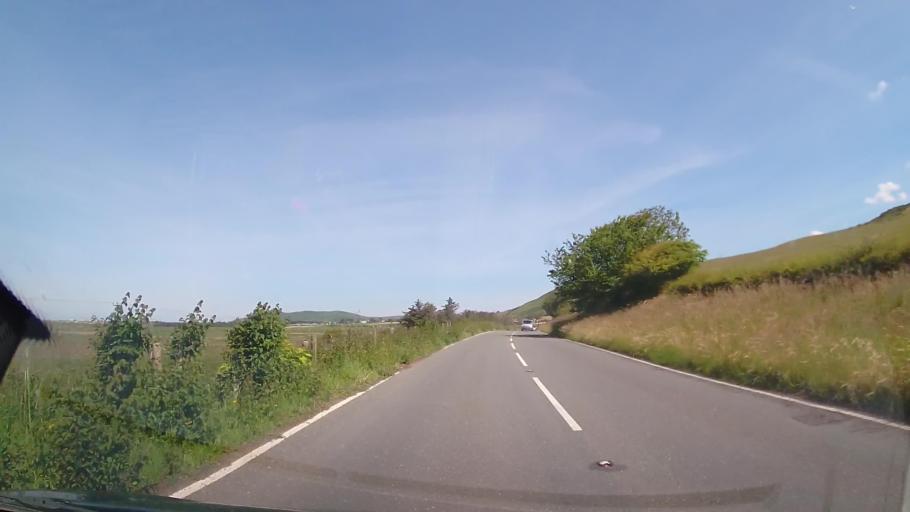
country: GB
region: Wales
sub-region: Gwynedd
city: Tywyn
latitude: 52.5650
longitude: -4.0724
